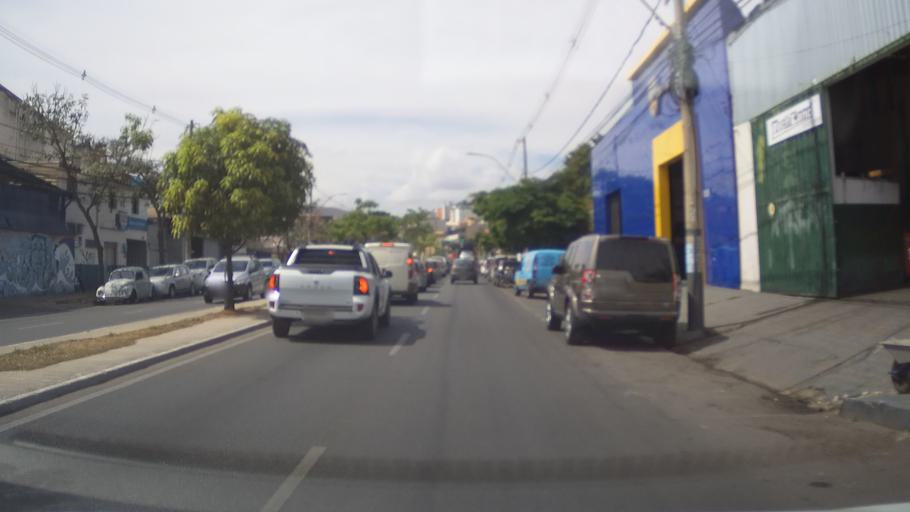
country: BR
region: Minas Gerais
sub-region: Belo Horizonte
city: Belo Horizonte
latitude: -19.9463
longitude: -43.9695
